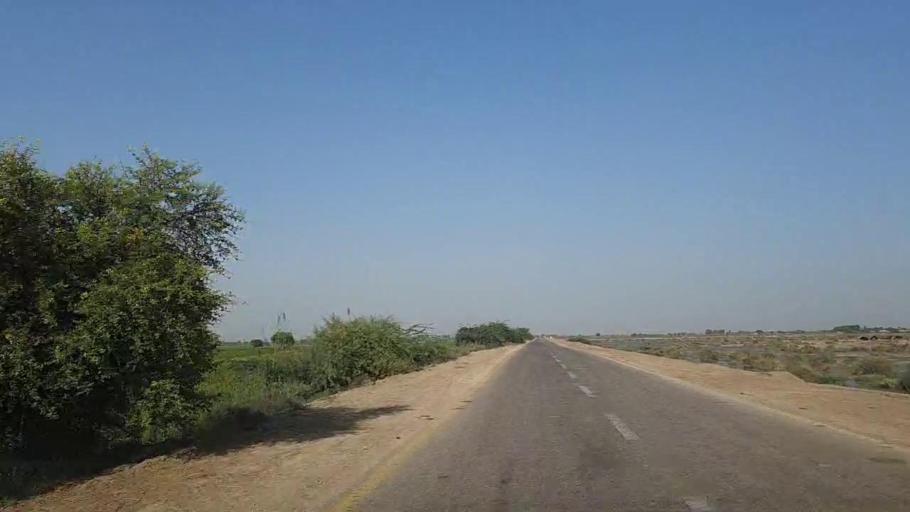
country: PK
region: Sindh
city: Jati
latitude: 24.3964
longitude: 68.2908
